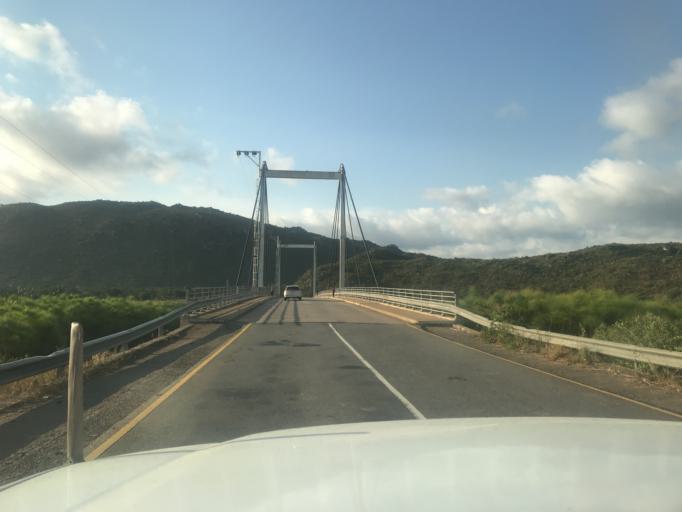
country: TZ
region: Mara
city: Musoma
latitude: -1.5300
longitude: 33.9751
